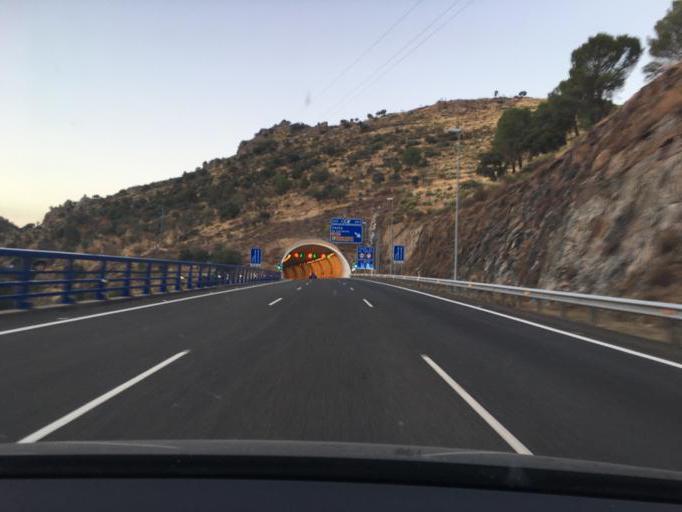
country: ES
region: Andalusia
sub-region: Provincia de Jaen
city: Santa Elena
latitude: 38.4009
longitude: -3.4984
